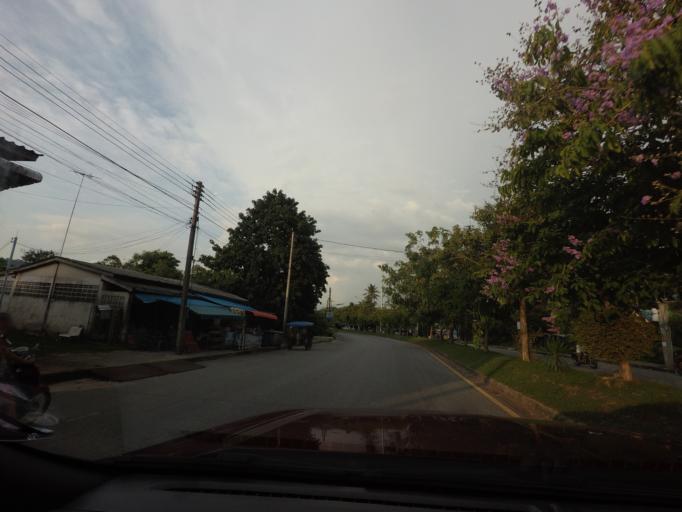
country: TH
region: Pattani
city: Khok Pho
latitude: 6.6771
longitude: 101.1441
